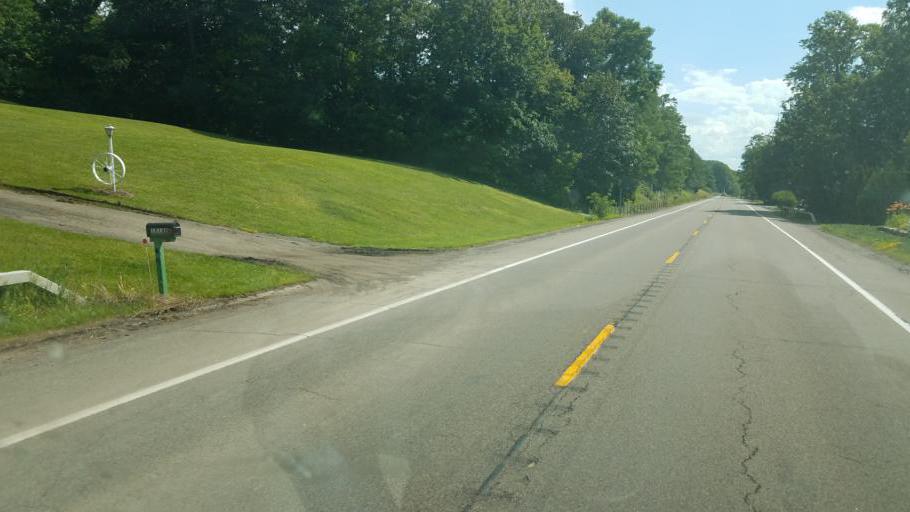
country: US
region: New York
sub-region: Steuben County
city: Sylvan Beach
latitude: 42.4989
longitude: -77.1121
